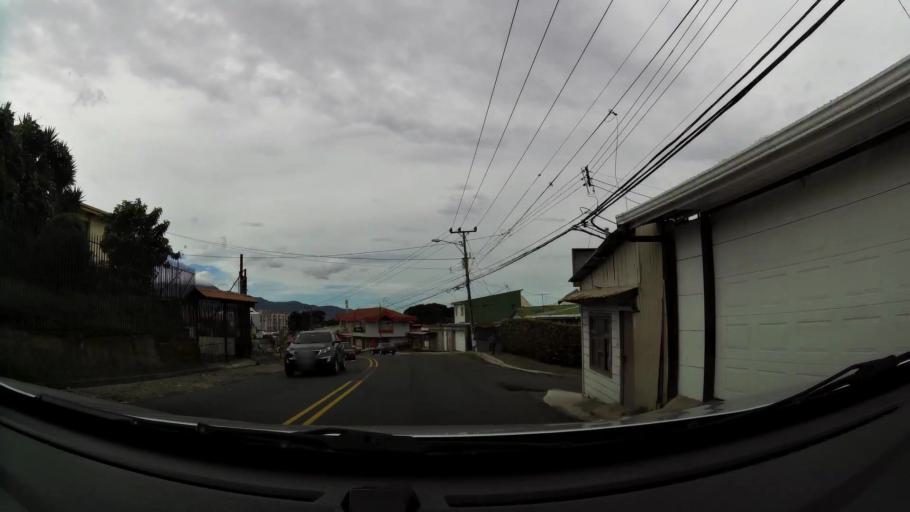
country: CR
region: San Jose
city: Sabanilla
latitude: 9.9440
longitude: -84.0391
